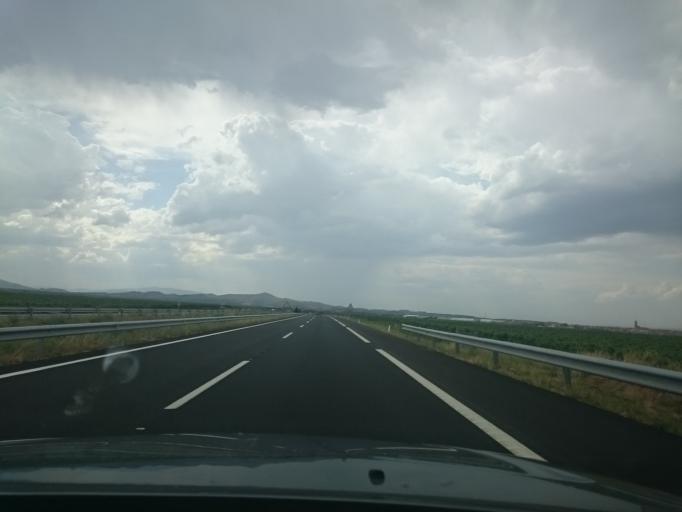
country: ES
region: La Rioja
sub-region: Provincia de La Rioja
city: Aldeanueva de Ebro
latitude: 42.2092
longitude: -1.8722
